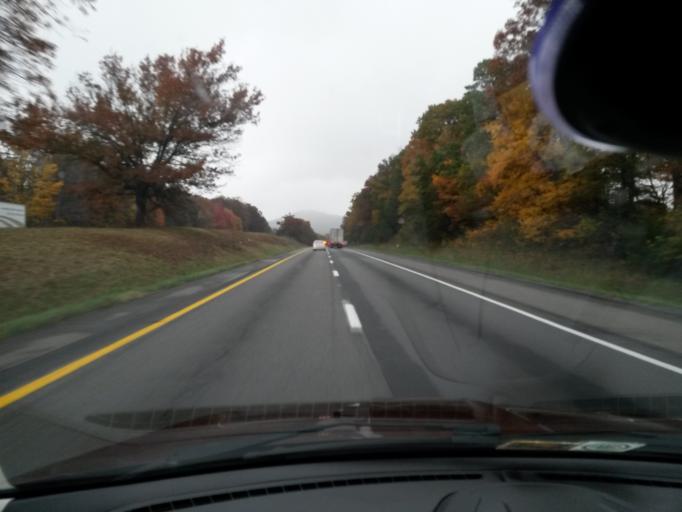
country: US
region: Virginia
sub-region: City of Salem
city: Salem
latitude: 37.2832
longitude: -80.1269
